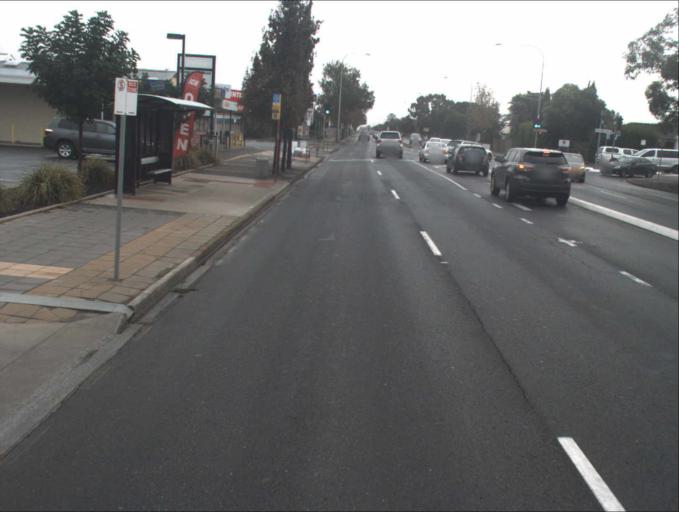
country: AU
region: South Australia
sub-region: Port Adelaide Enfield
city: Enfield
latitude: -34.8593
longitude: 138.6182
